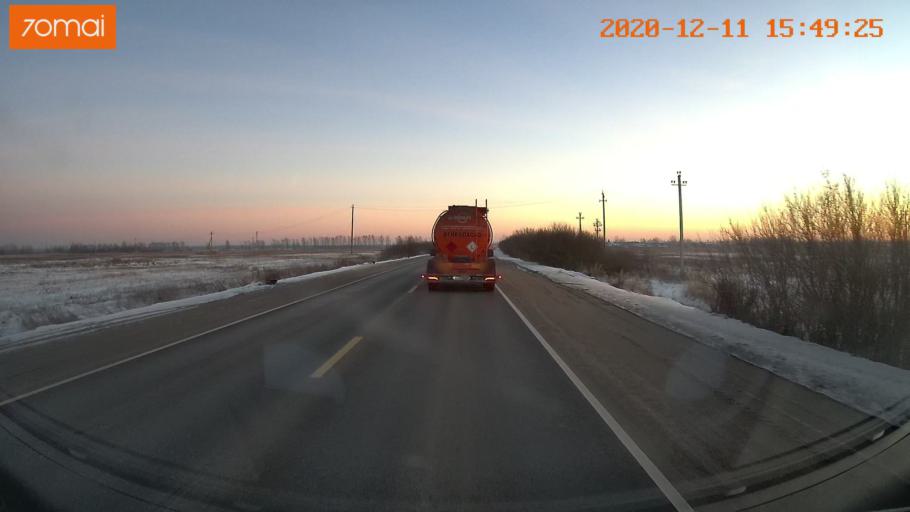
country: RU
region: Ivanovo
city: Novo-Talitsy
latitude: 56.9881
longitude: 40.8743
